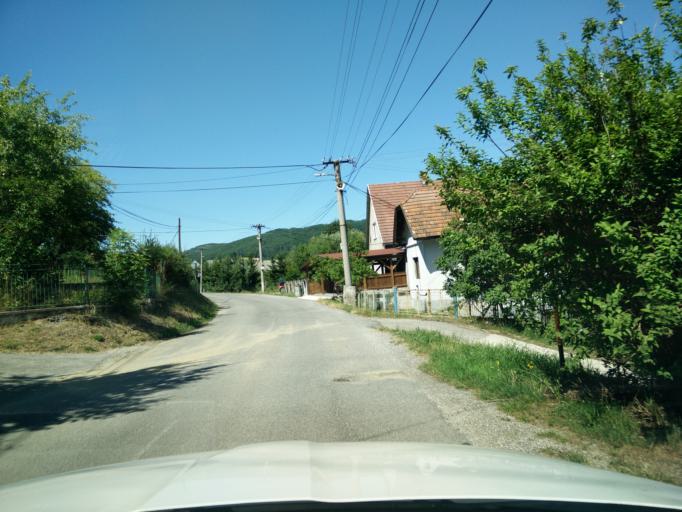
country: SK
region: Nitriansky
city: Prievidza
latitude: 48.7918
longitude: 18.6991
